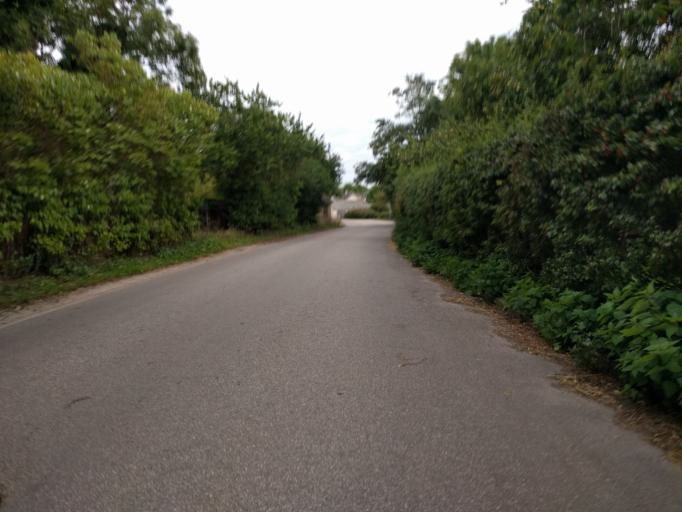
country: DK
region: South Denmark
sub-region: Odense Kommune
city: Bullerup
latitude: 55.4360
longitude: 10.5090
